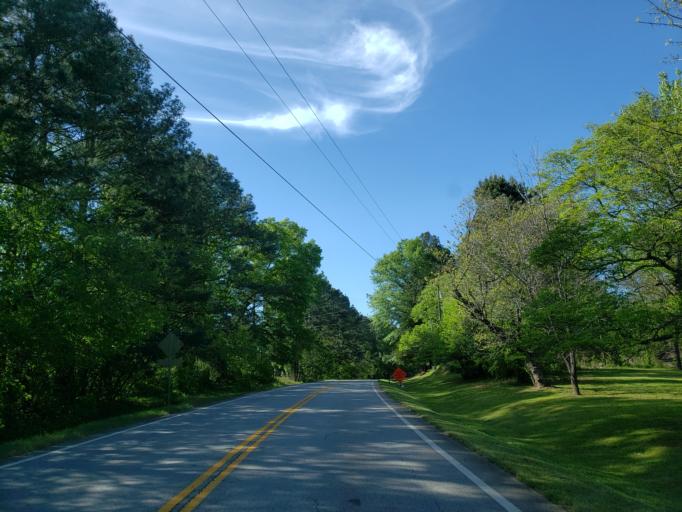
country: US
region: Georgia
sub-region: Haralson County
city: Tallapoosa
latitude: 33.7014
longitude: -85.2696
